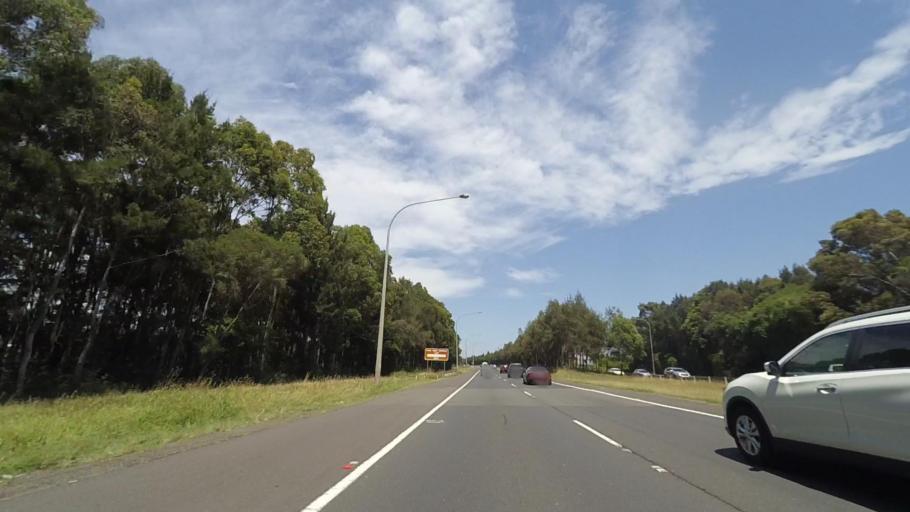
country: AU
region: New South Wales
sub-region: Wollongong
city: Mount Saint Thomas
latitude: -34.4421
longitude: 150.8636
